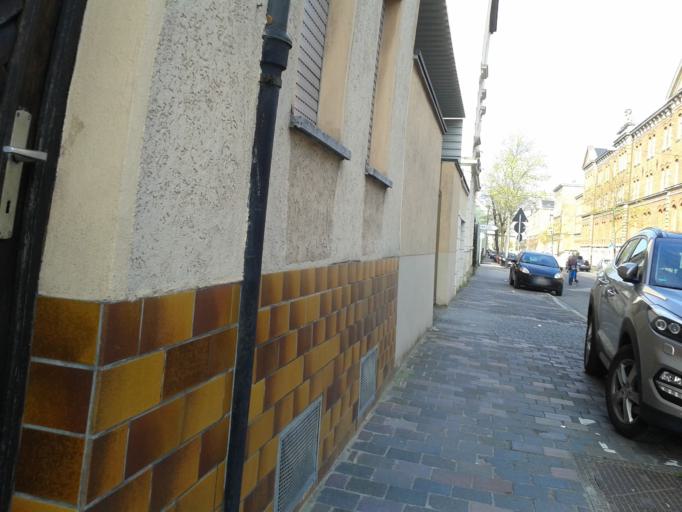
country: DE
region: Bavaria
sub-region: Upper Franconia
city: Bamberg
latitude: 49.9013
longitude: 10.9172
